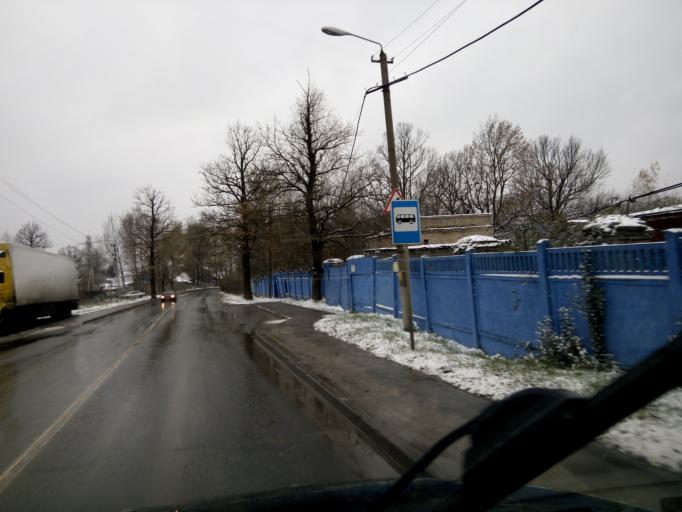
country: RU
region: Moskovskaya
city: Skhodnya
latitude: 55.9411
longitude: 37.2763
